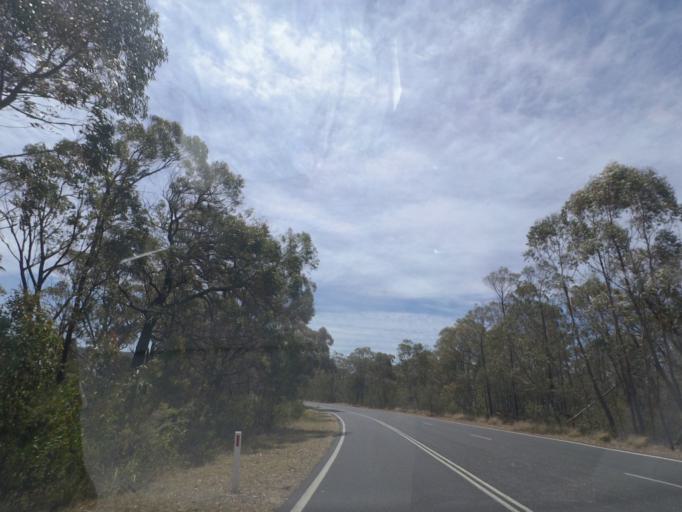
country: AU
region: New South Wales
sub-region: Wingecarribee
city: Colo Vale
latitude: -34.3961
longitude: 150.5331
